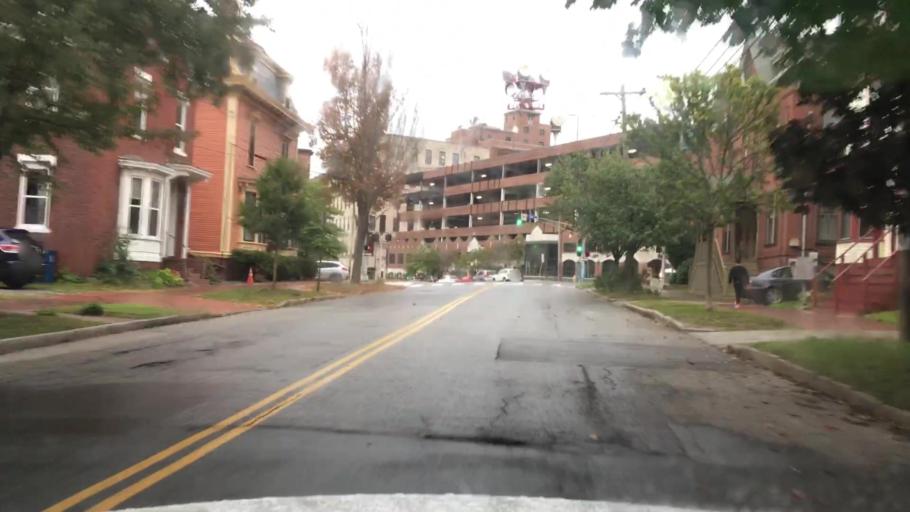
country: US
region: Maine
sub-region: Cumberland County
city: Portland
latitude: 43.6554
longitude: -70.2663
